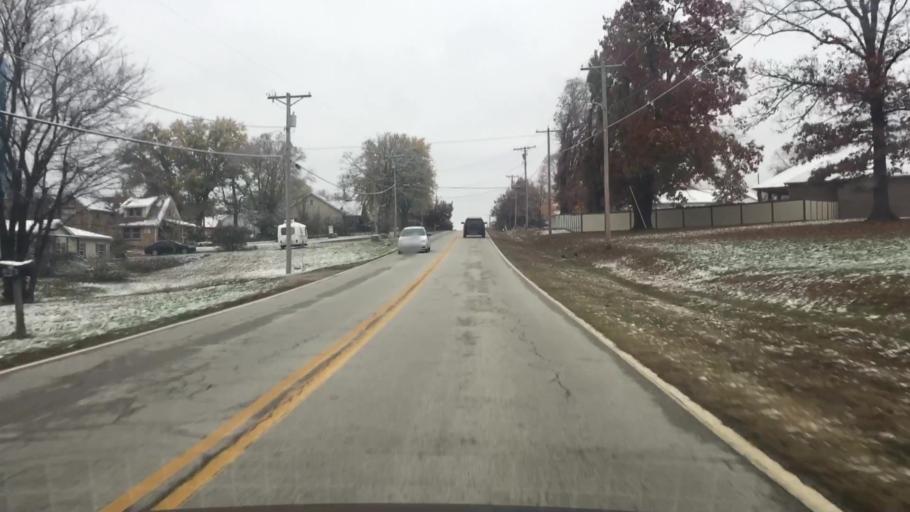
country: US
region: Missouri
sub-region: Saint Clair County
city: Osceola
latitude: 38.0334
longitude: -93.7028
